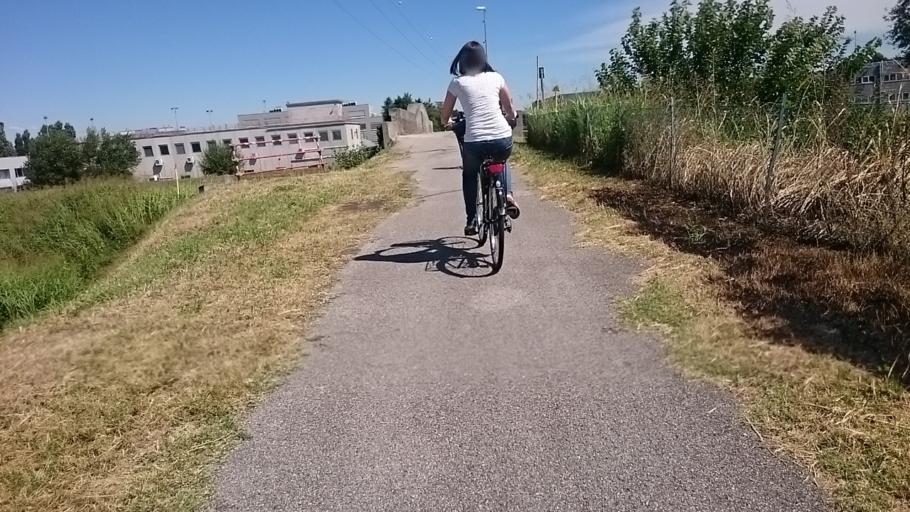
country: IT
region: Veneto
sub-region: Provincia di Padova
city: Noventa
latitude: 45.4063
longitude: 11.9369
